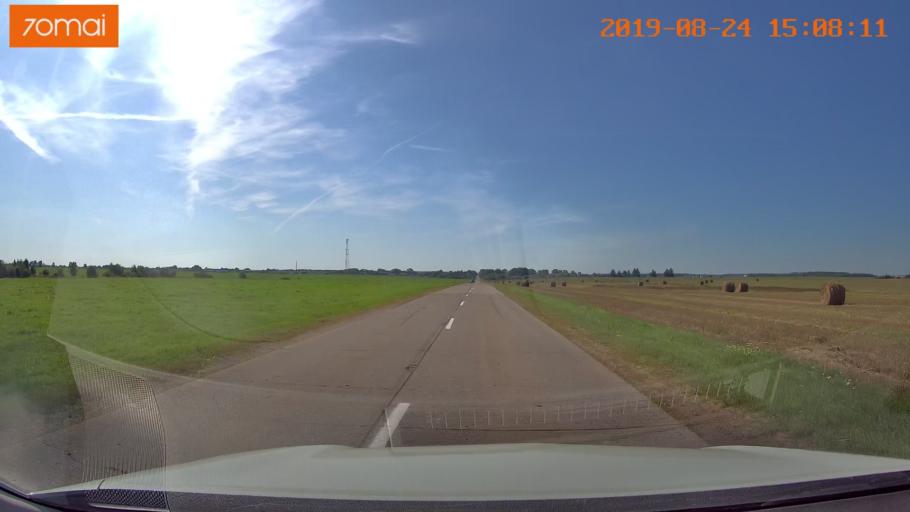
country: BY
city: Michanovichi
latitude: 53.6084
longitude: 27.6620
